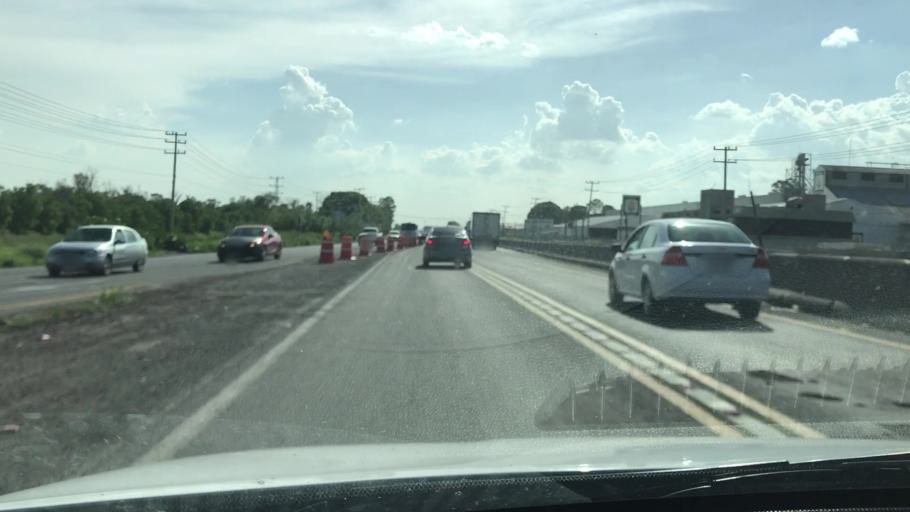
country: MX
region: Guanajuato
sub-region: Celaya
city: Colonia Fraccionamiento el Puente
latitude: 20.5145
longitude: -100.9062
